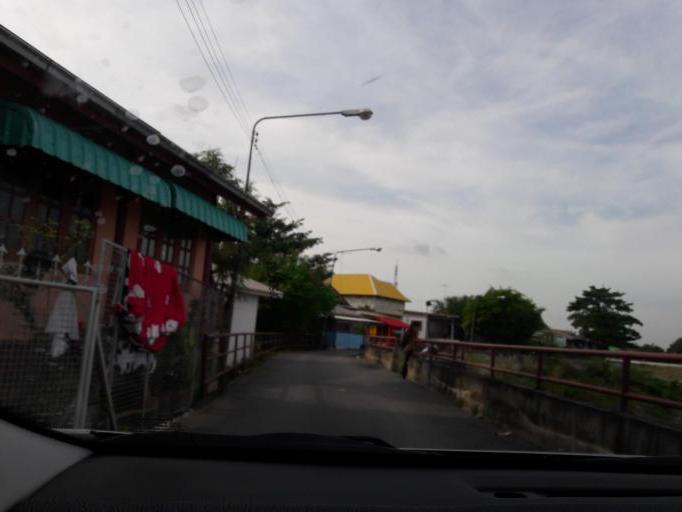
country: TH
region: Ang Thong
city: Ang Thong
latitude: 14.5893
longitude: 100.4580
